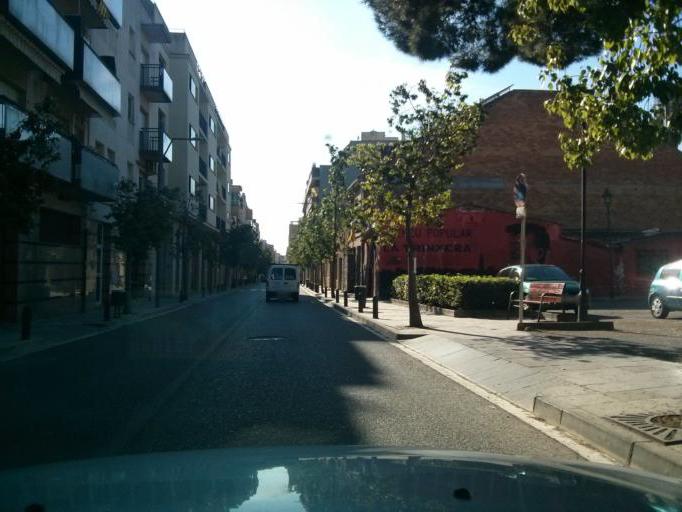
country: ES
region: Catalonia
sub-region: Provincia de Tarragona
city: El Vendrell
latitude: 41.2254
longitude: 1.5381
